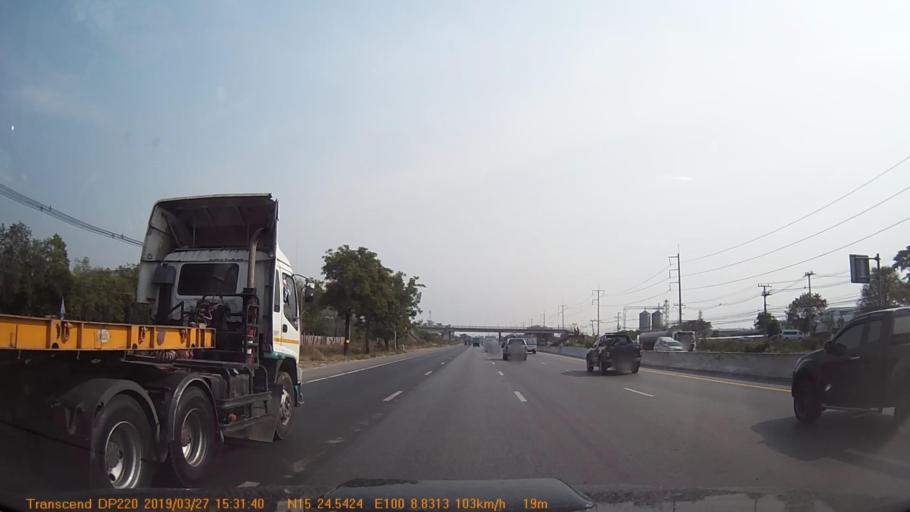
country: TH
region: Nakhon Sawan
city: Phayuha Khiri
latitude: 15.4106
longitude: 100.1444
